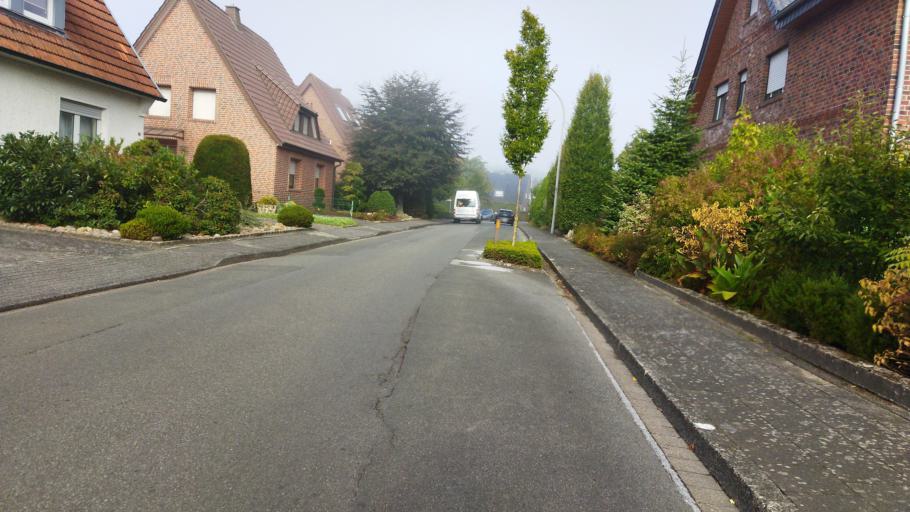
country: DE
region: North Rhine-Westphalia
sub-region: Regierungsbezirk Munster
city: Wettringen
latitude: 52.2199
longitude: 7.3357
